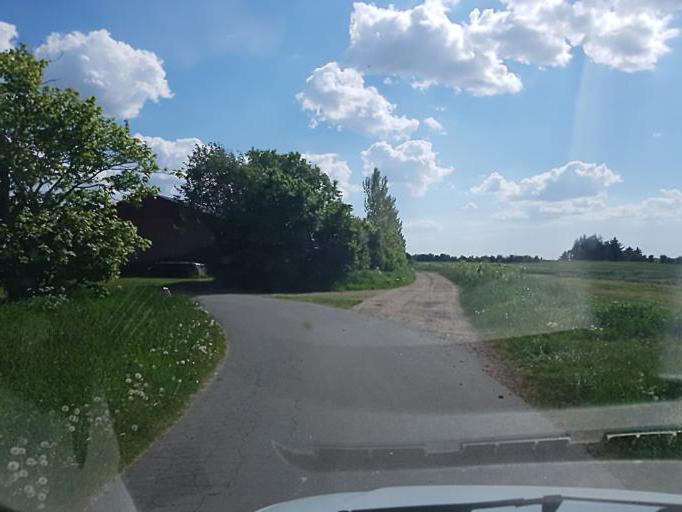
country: DK
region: South Denmark
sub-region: Esbjerg Kommune
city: Tjaereborg
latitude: 55.4244
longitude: 8.6387
